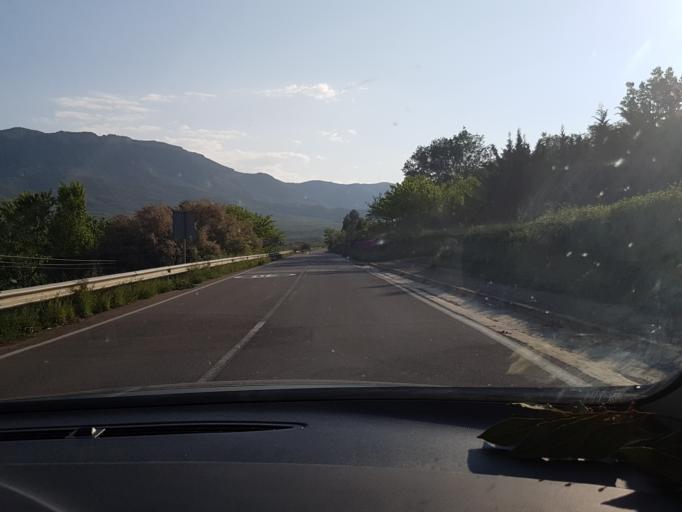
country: ES
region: La Rioja
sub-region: Provincia de La Rioja
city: Herce
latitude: 42.2138
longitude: -2.1683
